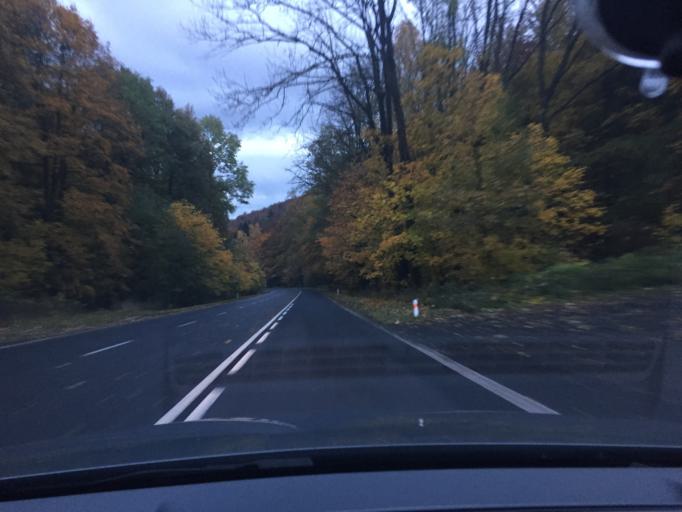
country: CZ
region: Ustecky
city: Dubi
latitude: 50.6989
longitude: 13.7634
